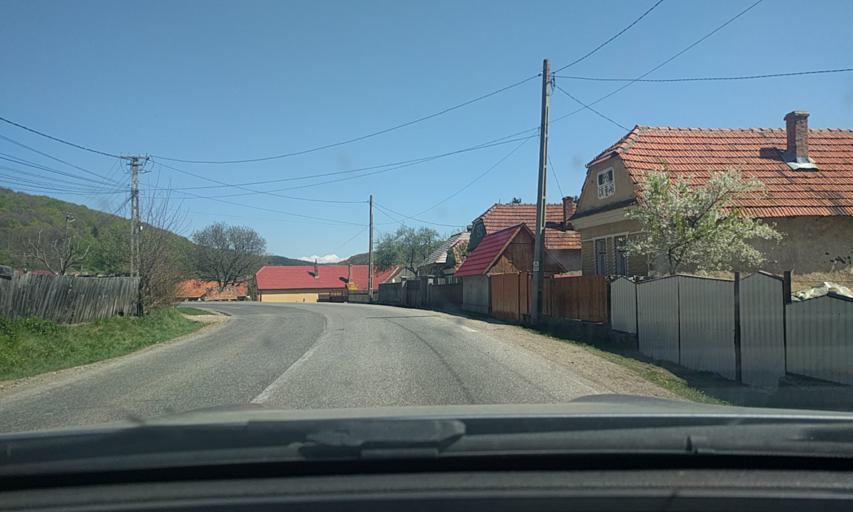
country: RO
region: Brasov
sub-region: Comuna Teliu
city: Teliu
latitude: 45.6822
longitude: 25.9116
